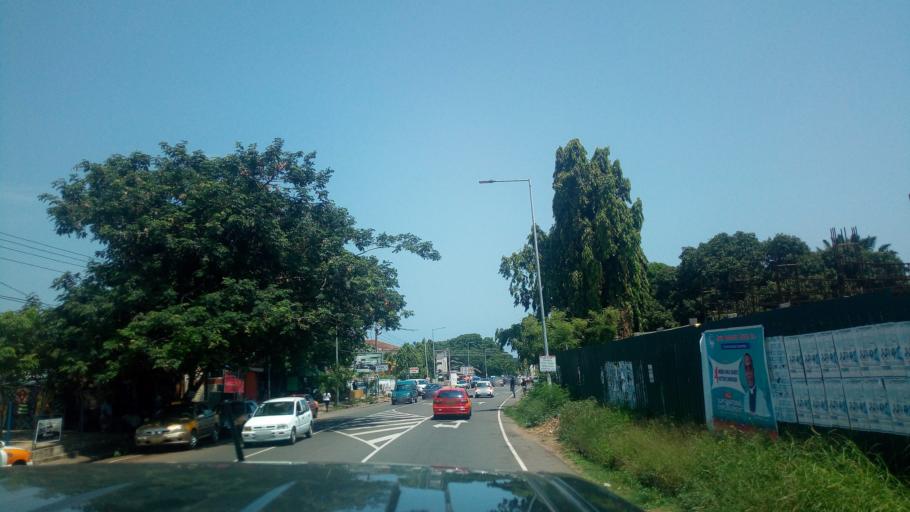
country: GH
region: Greater Accra
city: Accra
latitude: 5.5695
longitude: -0.1687
